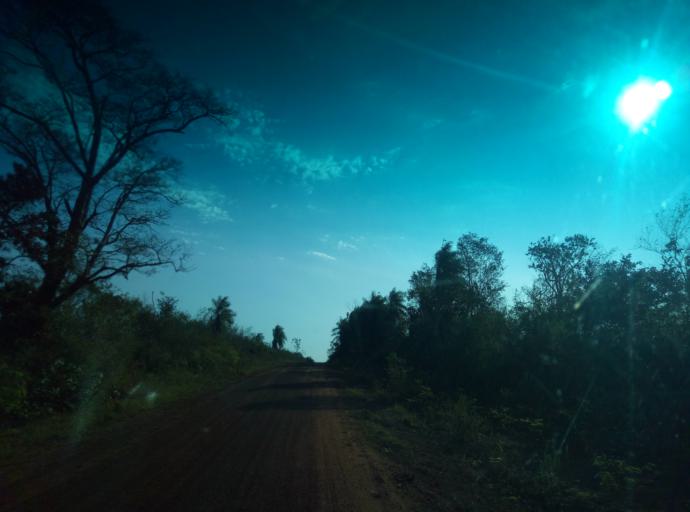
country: PY
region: Caaguazu
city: Doctor Cecilio Baez
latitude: -25.1648
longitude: -56.2283
